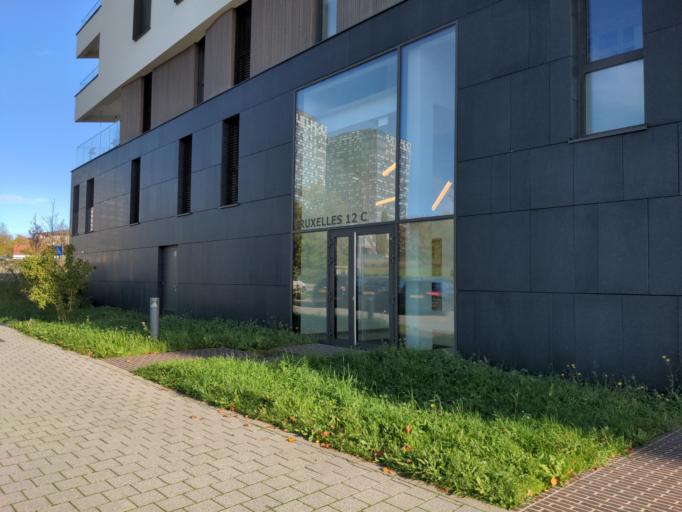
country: LU
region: Luxembourg
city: Kirchberg
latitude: 49.6357
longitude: 6.1611
